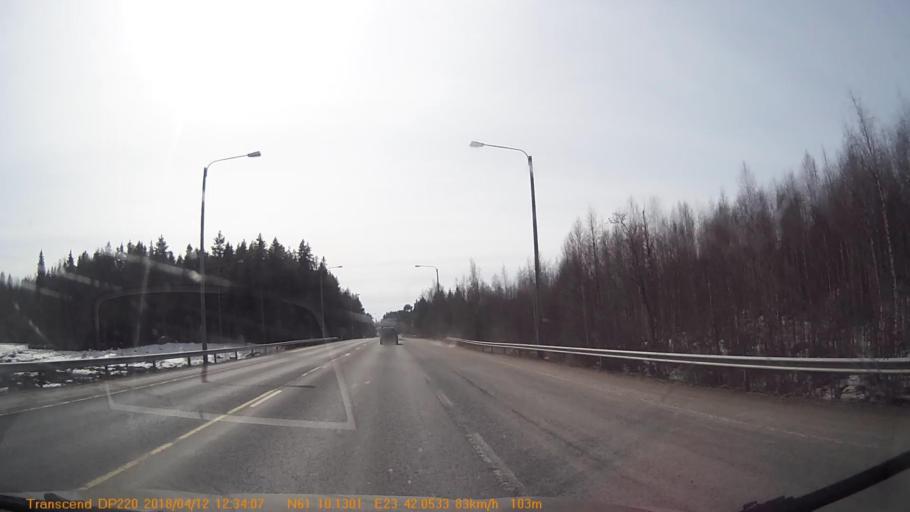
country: FI
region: Pirkanmaa
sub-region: Etelae-Pirkanmaa
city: Kylmaekoski
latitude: 61.1685
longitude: 23.7006
